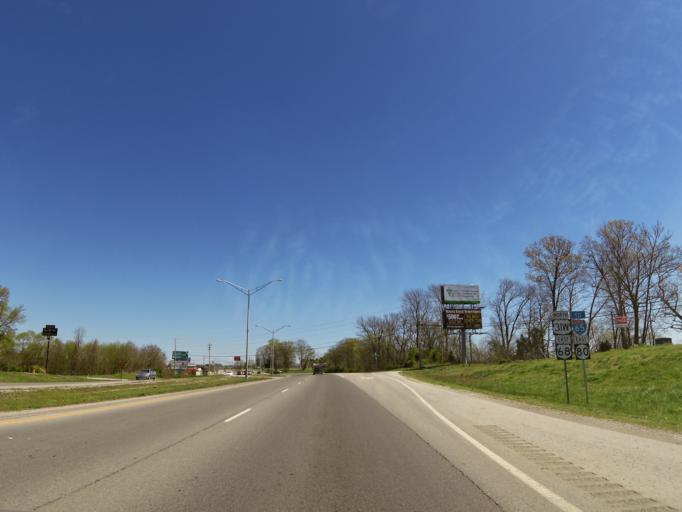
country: US
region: Kentucky
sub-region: Warren County
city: Bowling Green
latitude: 37.0088
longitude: -86.4068
